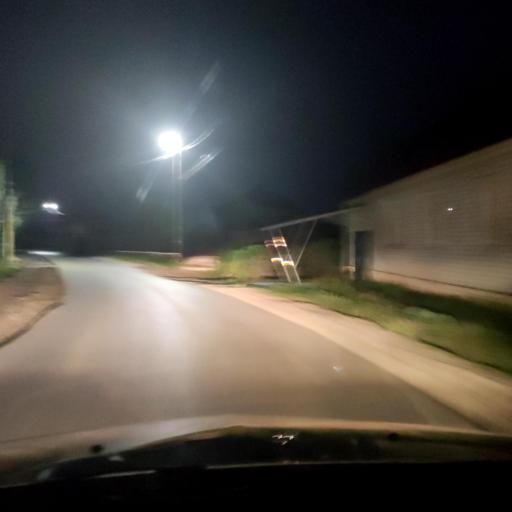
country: RU
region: Voronezj
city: Novaya Usman'
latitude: 51.6391
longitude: 39.3959
